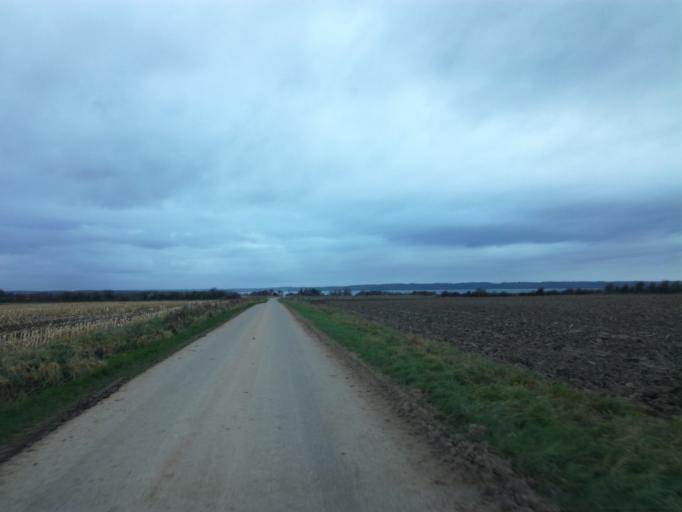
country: DK
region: South Denmark
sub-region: Fredericia Kommune
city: Fredericia
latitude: 55.6100
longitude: 9.7806
